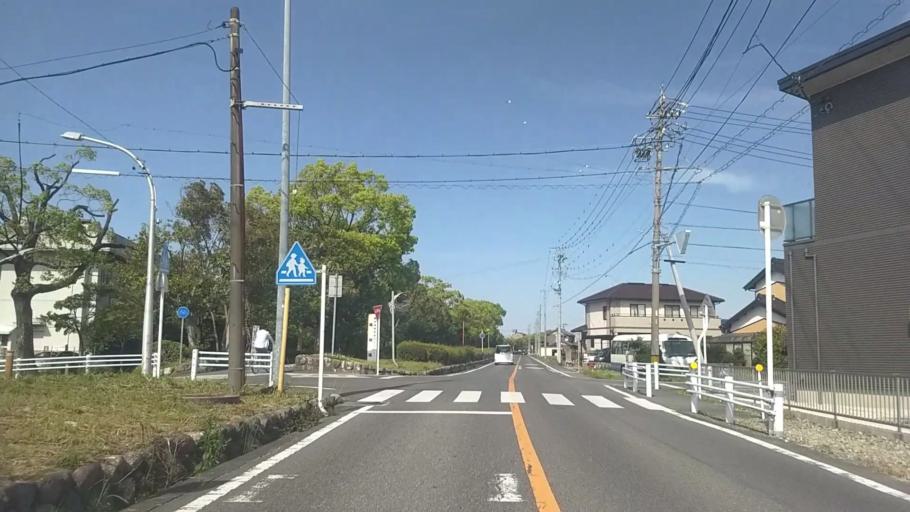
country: JP
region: Aichi
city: Anjo
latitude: 34.9742
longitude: 137.0774
